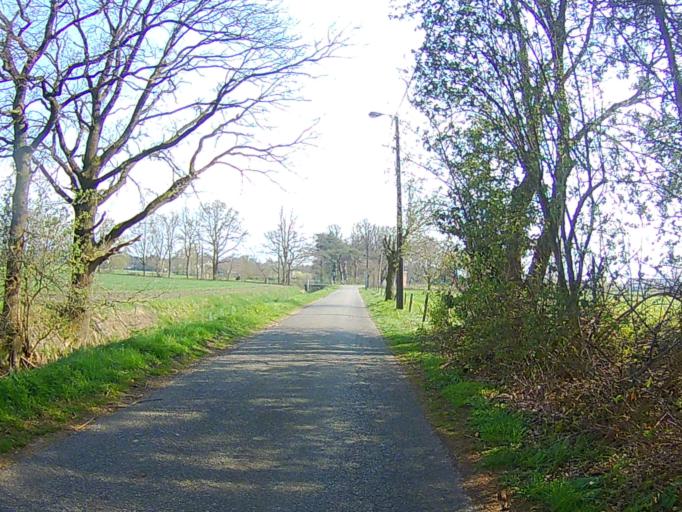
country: BE
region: Flanders
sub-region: Provincie Antwerpen
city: Essen
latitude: 51.4618
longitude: 4.5061
